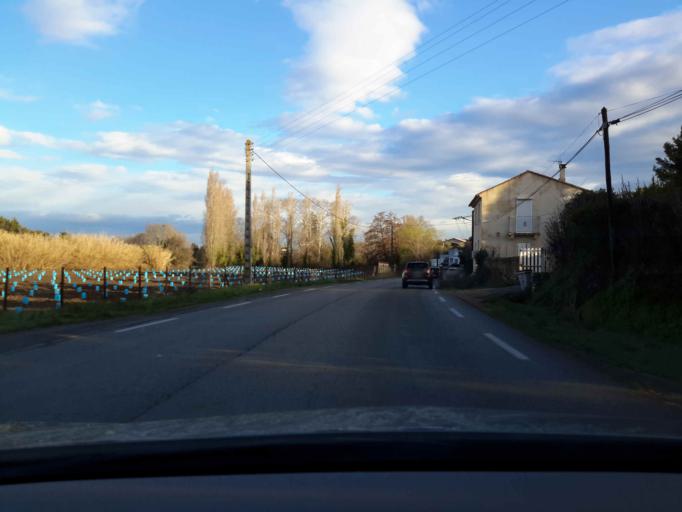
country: FR
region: Languedoc-Roussillon
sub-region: Departement du Gard
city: Generac
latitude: 43.7404
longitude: 4.3429
